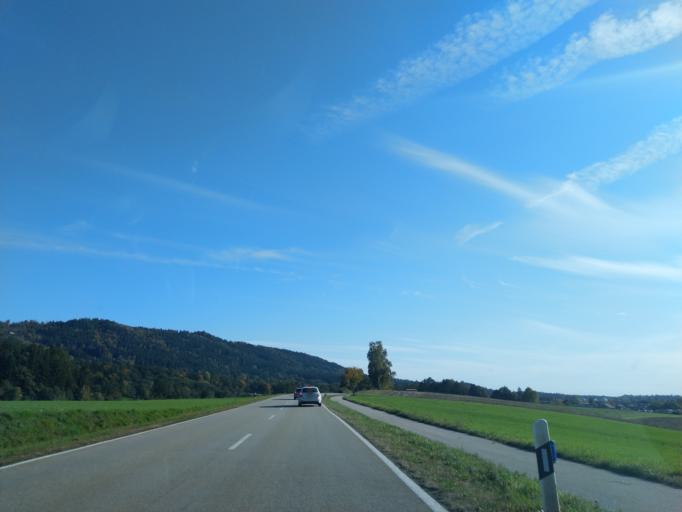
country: DE
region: Bavaria
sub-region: Lower Bavaria
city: Bernried
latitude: 48.9057
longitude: 12.9222
